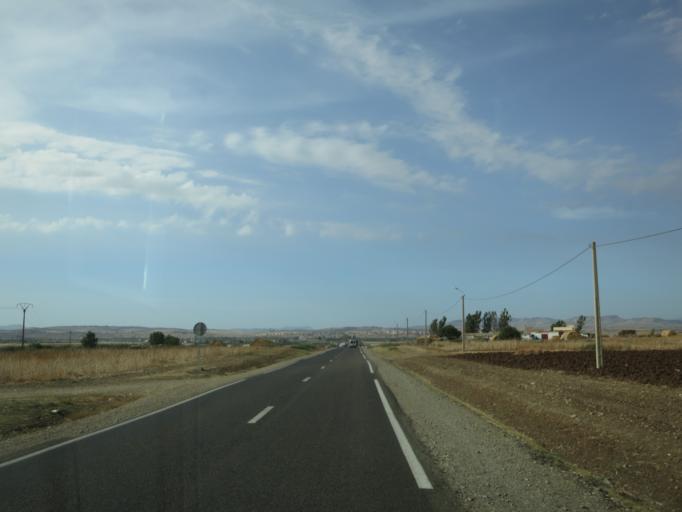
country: MA
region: Gharb-Chrarda-Beni Hssen
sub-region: Sidi-Kacem
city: Sidi Bousber
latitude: 34.4386
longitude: -5.5051
